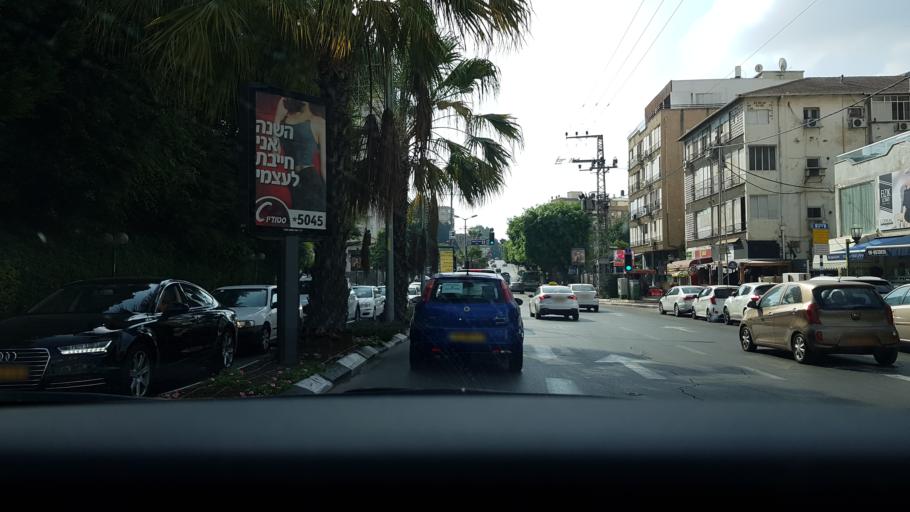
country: IL
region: Central District
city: Ness Ziona
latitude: 31.9033
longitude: 34.8080
